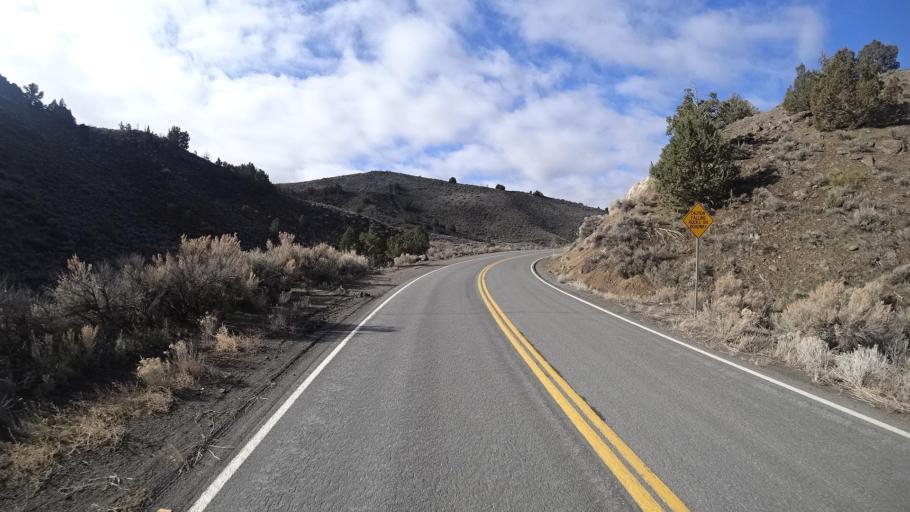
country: US
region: Nevada
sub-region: Washoe County
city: Cold Springs
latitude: 39.9032
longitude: -119.9951
